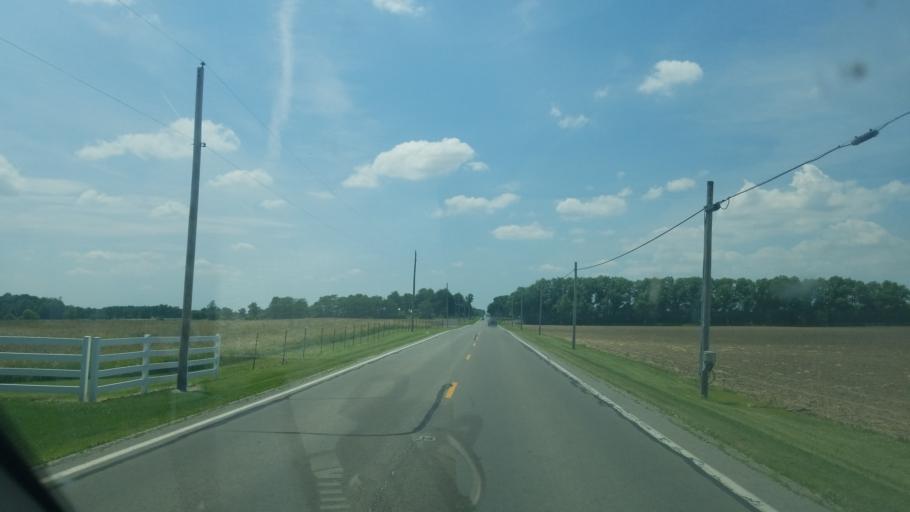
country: US
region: Ohio
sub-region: Hardin County
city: Ada
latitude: 40.7766
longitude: -83.8461
